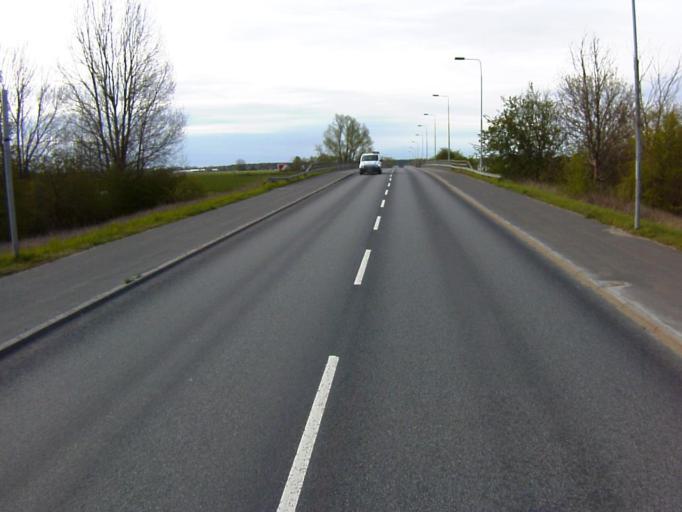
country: SE
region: Skane
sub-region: Kristianstads Kommun
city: Kristianstad
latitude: 56.0180
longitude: 14.1244
